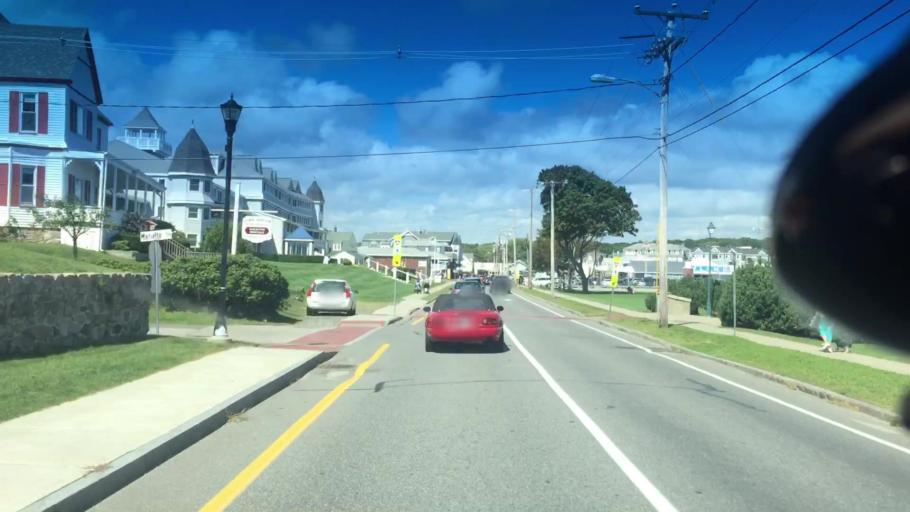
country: US
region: Maine
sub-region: York County
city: York Beach
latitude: 43.1731
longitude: -70.6077
